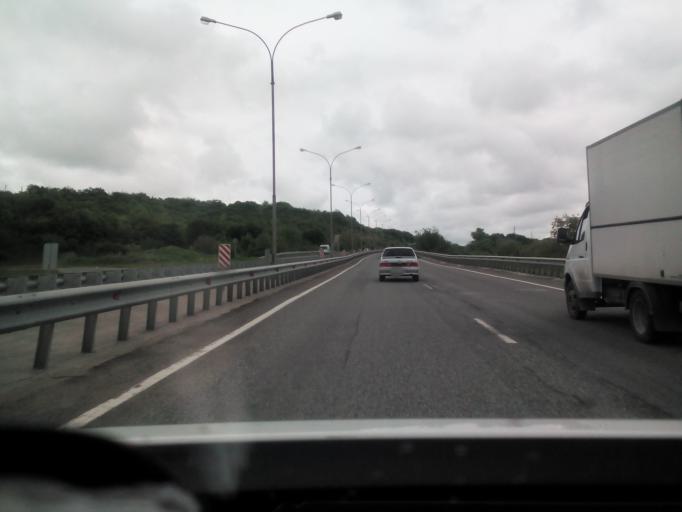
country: RU
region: Stavropol'skiy
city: Yasnaya Polyana
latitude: 44.0132
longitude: 42.7989
